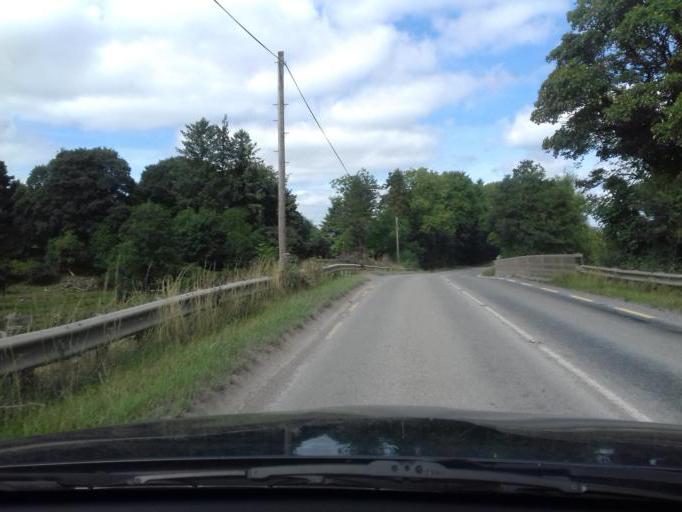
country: IE
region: Leinster
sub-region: Wicklow
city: Baltinglass
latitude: 52.9971
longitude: -6.6472
